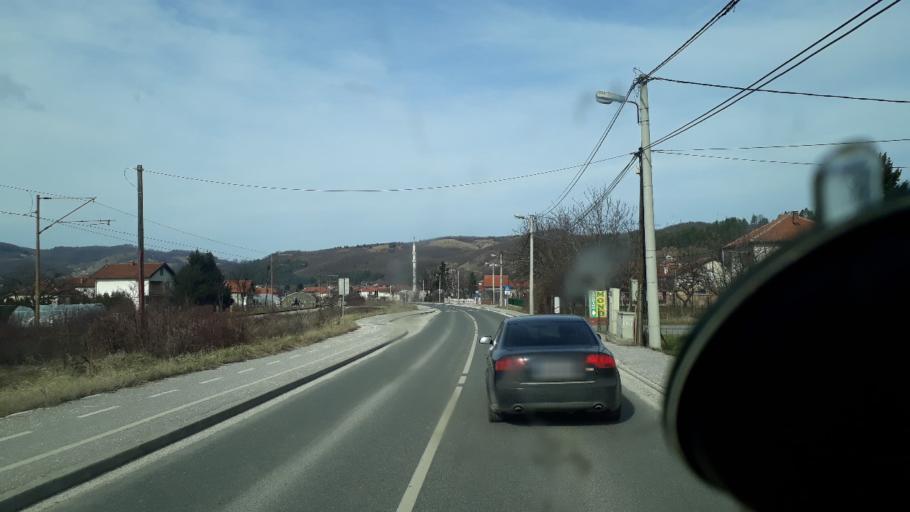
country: BA
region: Federation of Bosnia and Herzegovina
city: Mahala
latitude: 43.9821
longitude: 18.2394
